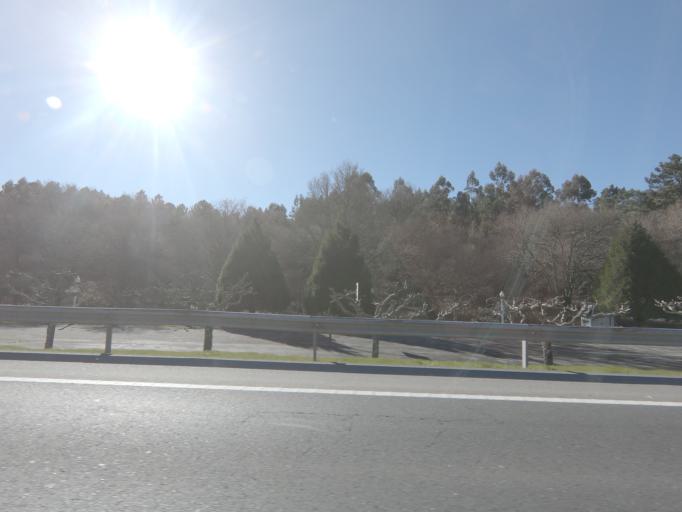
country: ES
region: Galicia
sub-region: Provincia de Pontevedra
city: Silleda
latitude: 42.6873
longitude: -8.2195
